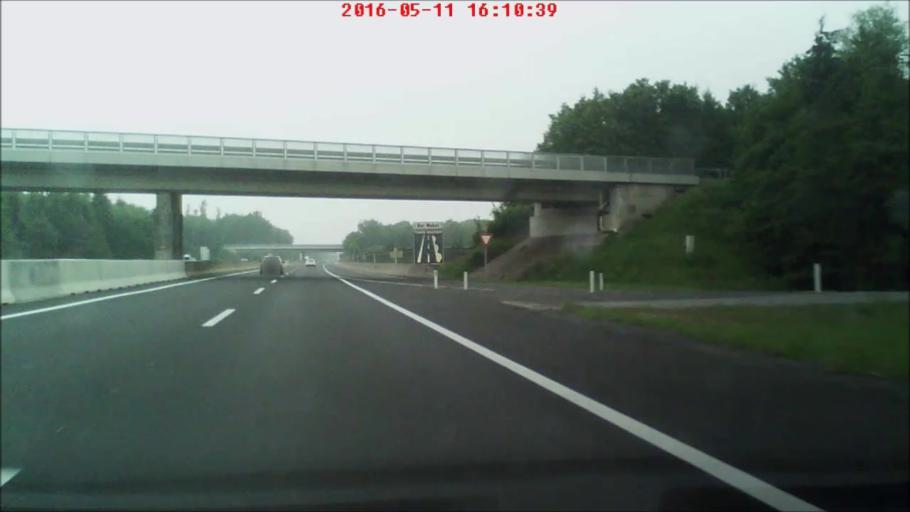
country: AT
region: Styria
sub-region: Politischer Bezirk Leibnitz
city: Kaindorf an der Sulm
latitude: 46.8103
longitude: 15.5673
